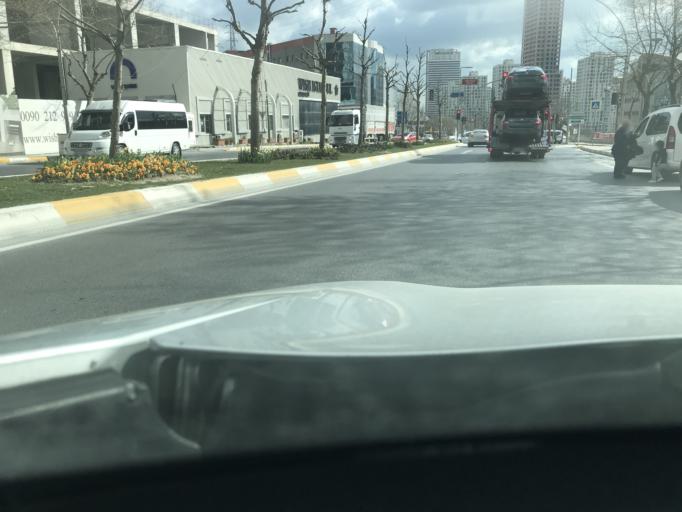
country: TR
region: Istanbul
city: Esenyurt
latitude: 41.0152
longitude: 28.6823
